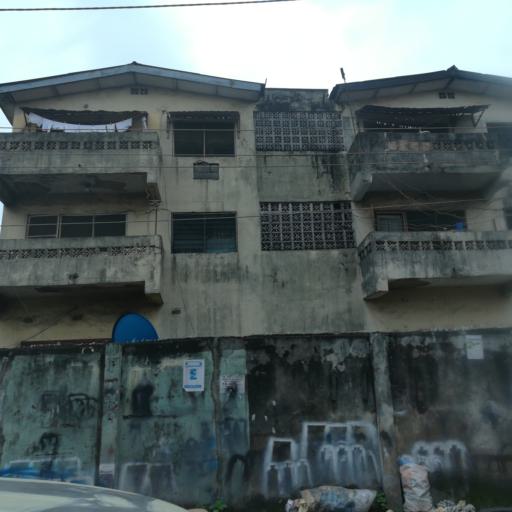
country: NG
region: Lagos
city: Ebute Metta
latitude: 6.4889
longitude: 3.3874
